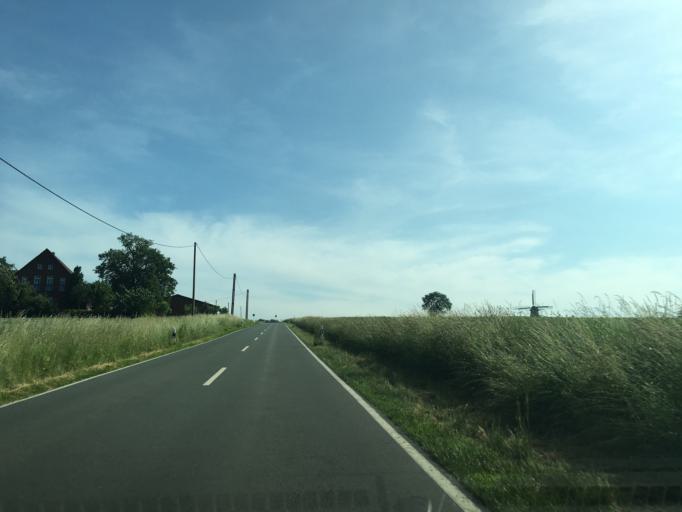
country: DE
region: North Rhine-Westphalia
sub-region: Regierungsbezirk Munster
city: Steinfurt
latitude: 52.1551
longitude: 7.3779
